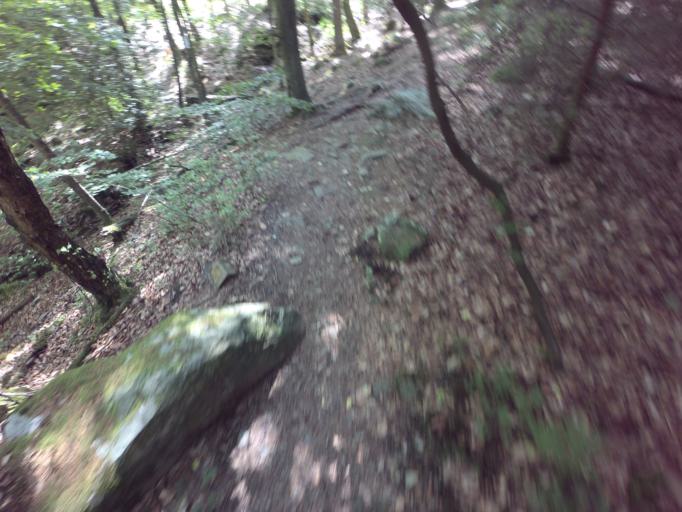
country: BE
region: Wallonia
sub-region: Province de Liege
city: Jalhay
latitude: 50.5188
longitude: 5.9819
